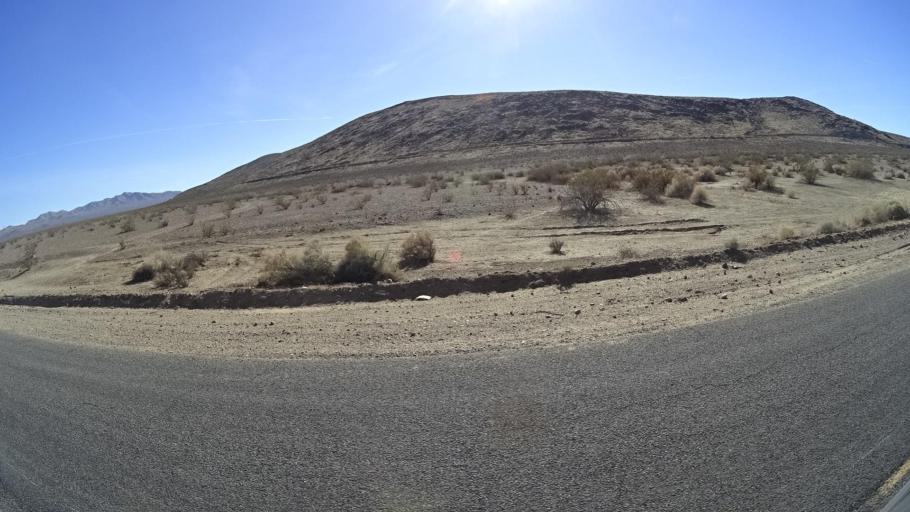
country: US
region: California
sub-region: Kern County
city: China Lake Acres
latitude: 35.5613
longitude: -117.7696
